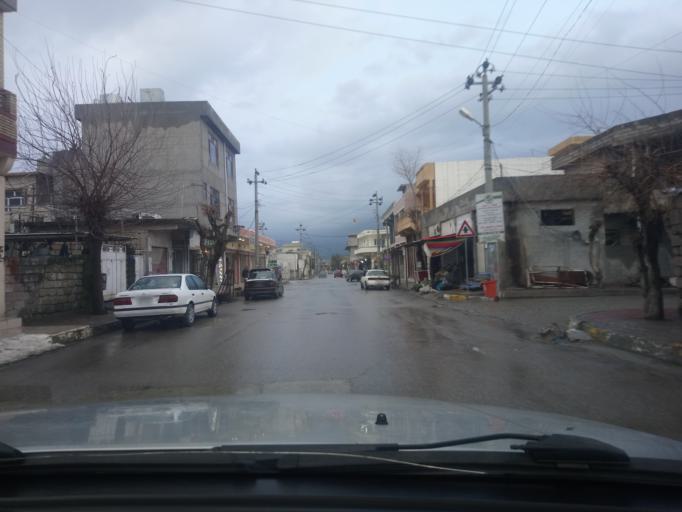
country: IQ
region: As Sulaymaniyah
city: Qeladize
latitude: 36.1866
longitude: 45.1265
